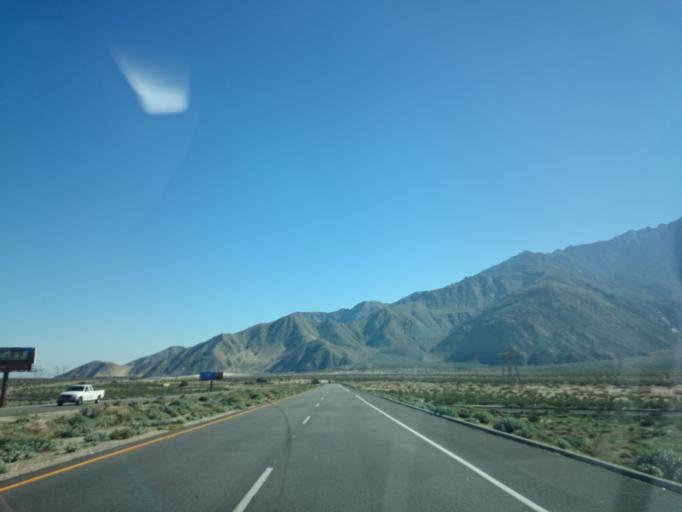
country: US
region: California
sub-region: Riverside County
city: Cabazon
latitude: 33.9199
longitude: -116.6759
